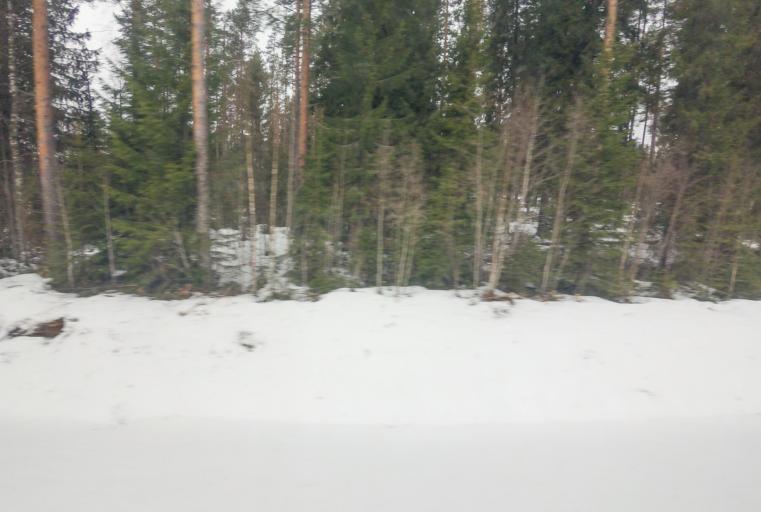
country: FI
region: South Karelia
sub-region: Imatra
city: Parikkala
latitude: 61.6296
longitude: 29.4318
